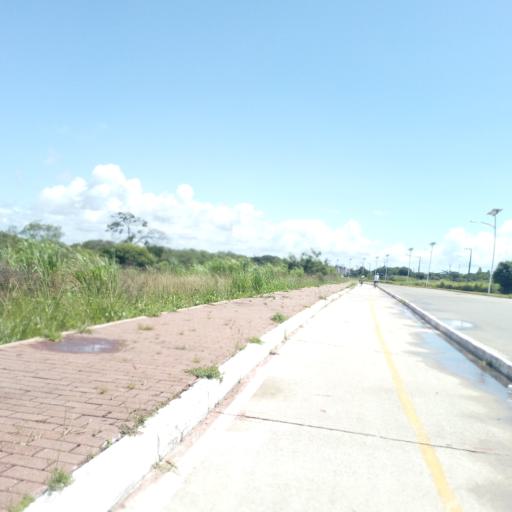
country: BR
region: Pernambuco
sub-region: Sirinhaem
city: Sirinhaem
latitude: -8.5169
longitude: -35.0100
